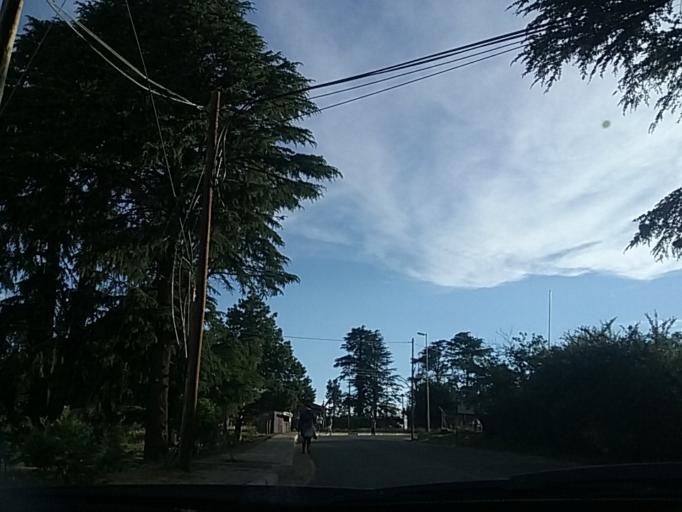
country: LS
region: Berea
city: Teyateyaneng
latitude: -29.1447
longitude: 27.7417
